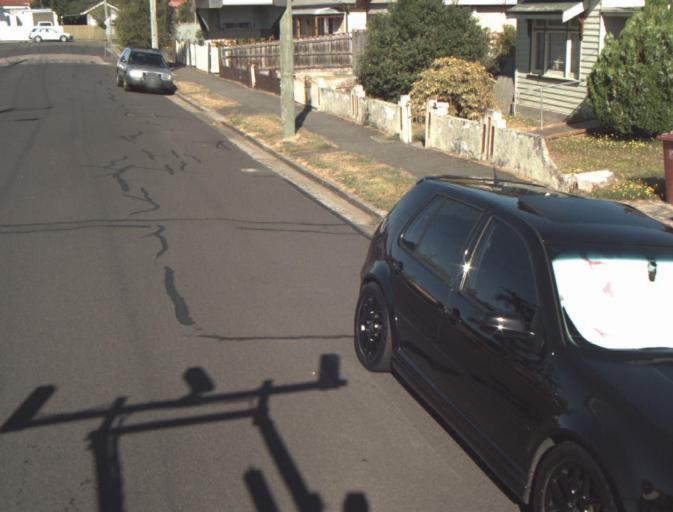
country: AU
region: Tasmania
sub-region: Launceston
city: Newnham
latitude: -41.4017
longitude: 147.1359
